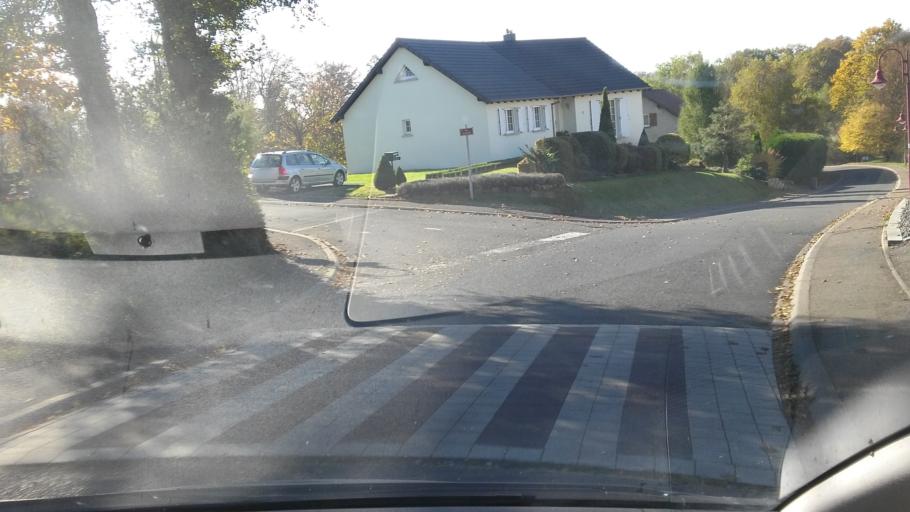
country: FR
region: Lorraine
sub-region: Departement de la Moselle
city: Phalsbourg
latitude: 48.7314
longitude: 7.2127
